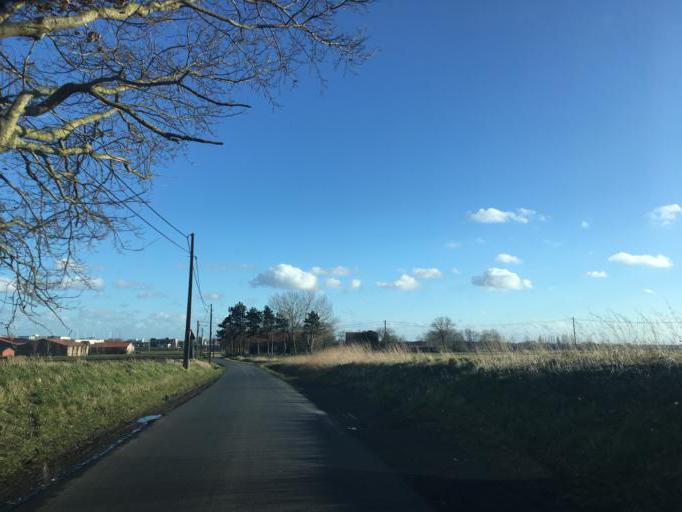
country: BE
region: Flanders
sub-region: Provincie West-Vlaanderen
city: Hooglede
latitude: 50.9853
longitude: 3.1100
